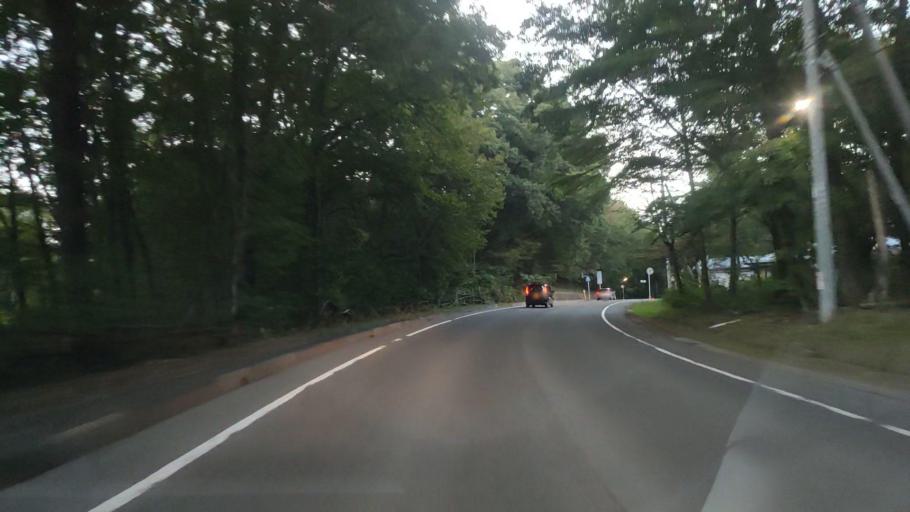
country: JP
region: Nagano
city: Komoro
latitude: 36.5024
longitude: 138.5900
